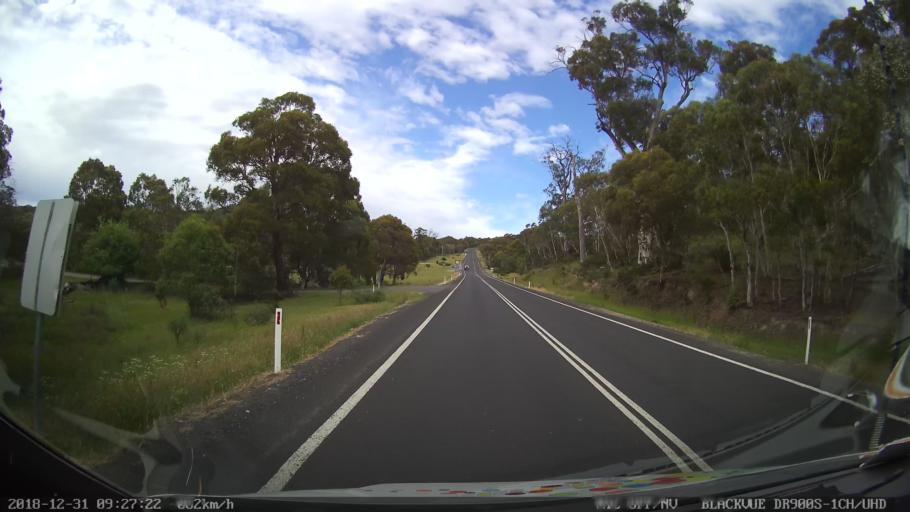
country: AU
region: New South Wales
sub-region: Snowy River
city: Jindabyne
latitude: -36.4557
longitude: 148.4855
